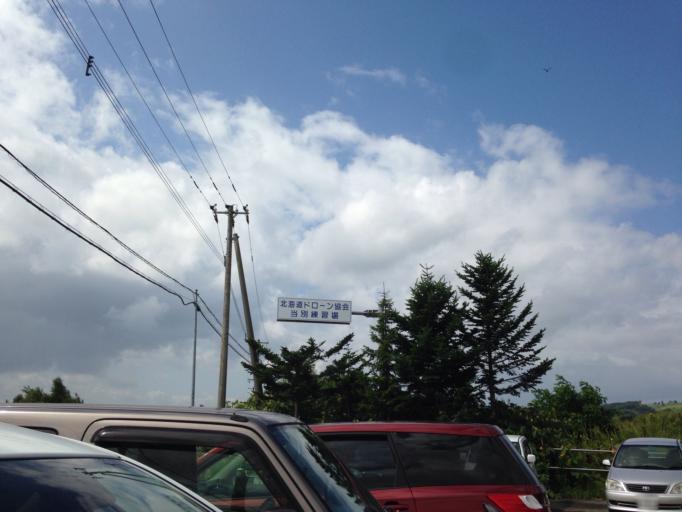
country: JP
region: Hokkaido
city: Tobetsu
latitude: 43.2568
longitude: 141.5294
